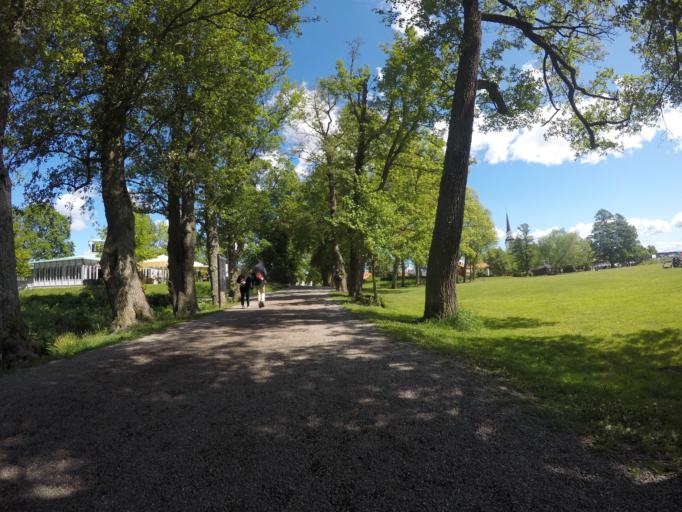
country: SE
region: Soedermanland
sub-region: Strangnas Kommun
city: Mariefred
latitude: 59.2579
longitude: 17.2188
